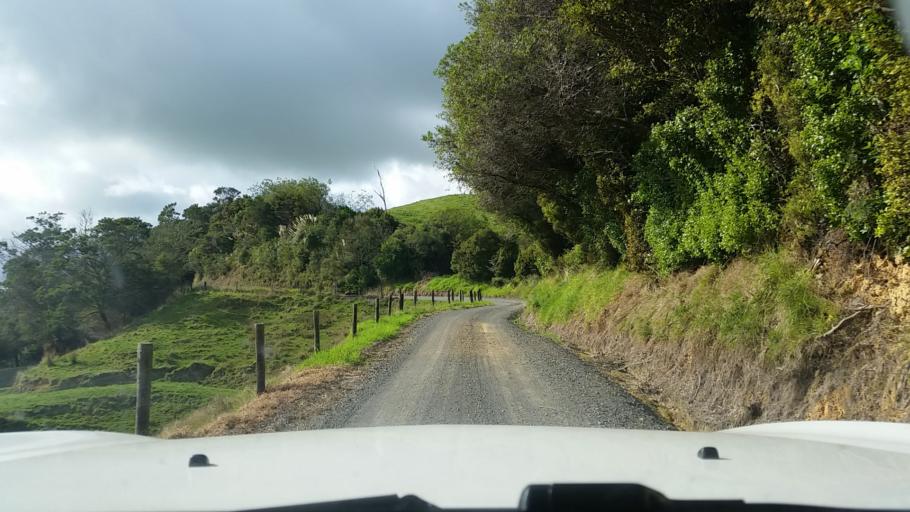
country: NZ
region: Waikato
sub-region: Hauraki District
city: Ngatea
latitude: -37.4660
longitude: 175.4598
